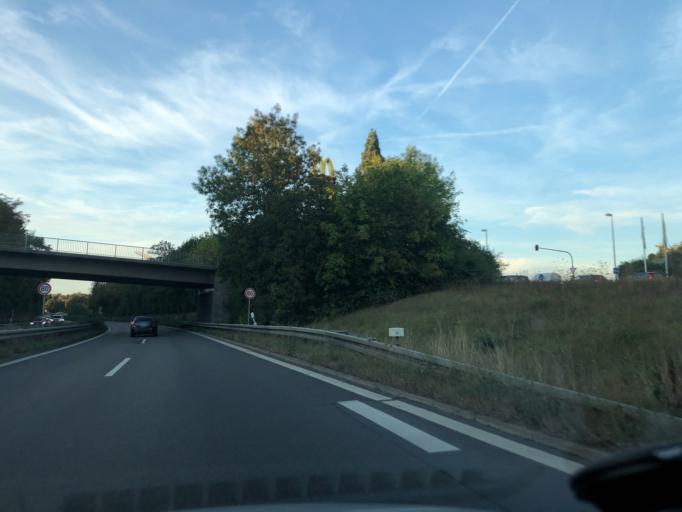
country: DE
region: Baden-Wuerttemberg
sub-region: Regierungsbezirk Stuttgart
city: Kornwestheim
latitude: 48.8659
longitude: 9.1974
